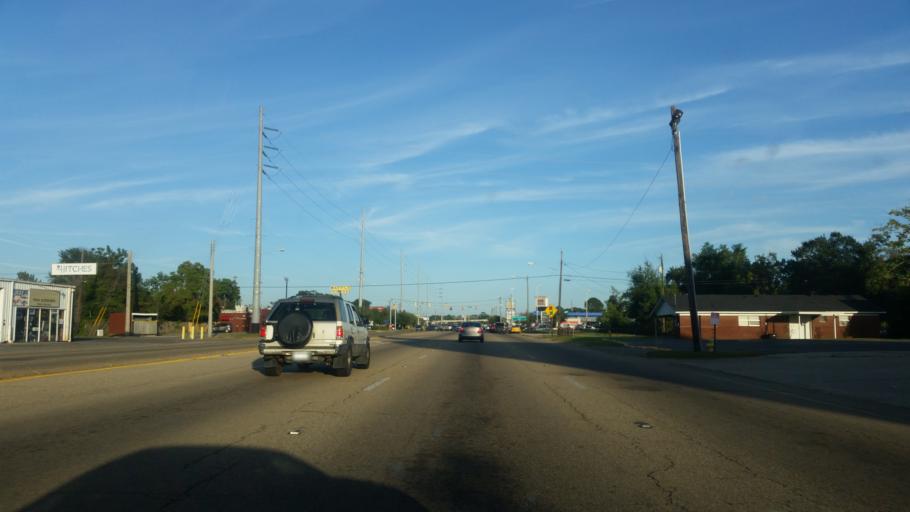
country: US
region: Mississippi
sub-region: Jackson County
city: Pascagoula
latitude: 30.3708
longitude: -88.5510
